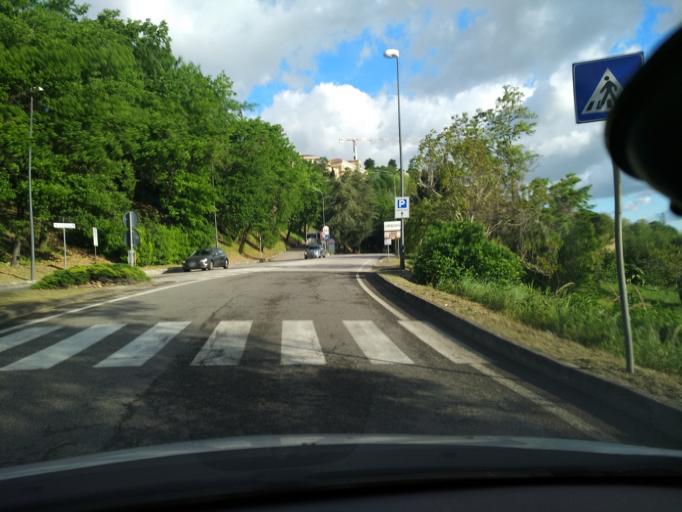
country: IT
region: The Marches
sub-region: Provincia di Pesaro e Urbino
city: Urbino
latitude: 43.7268
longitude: 12.6395
